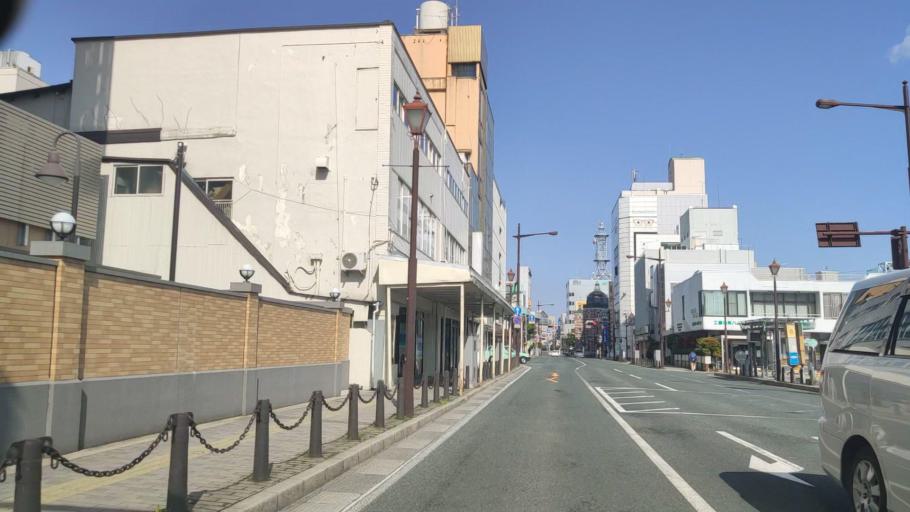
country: JP
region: Iwate
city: Morioka-shi
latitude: 39.6994
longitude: 141.1571
